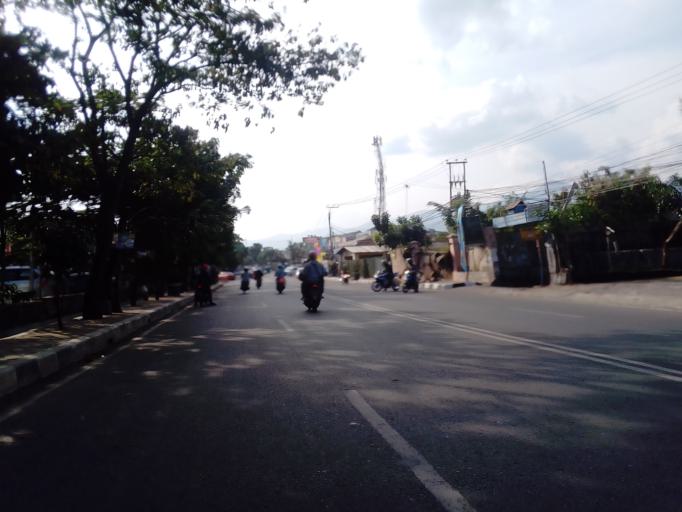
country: ID
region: West Java
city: Cileunyi
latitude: -6.9309
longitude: 107.7126
